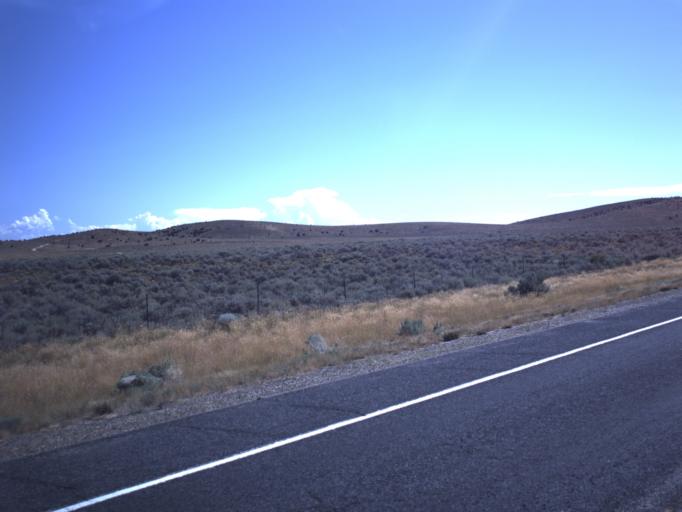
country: US
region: Utah
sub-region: Utah County
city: Eagle Mountain
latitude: 40.0765
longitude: -112.3898
